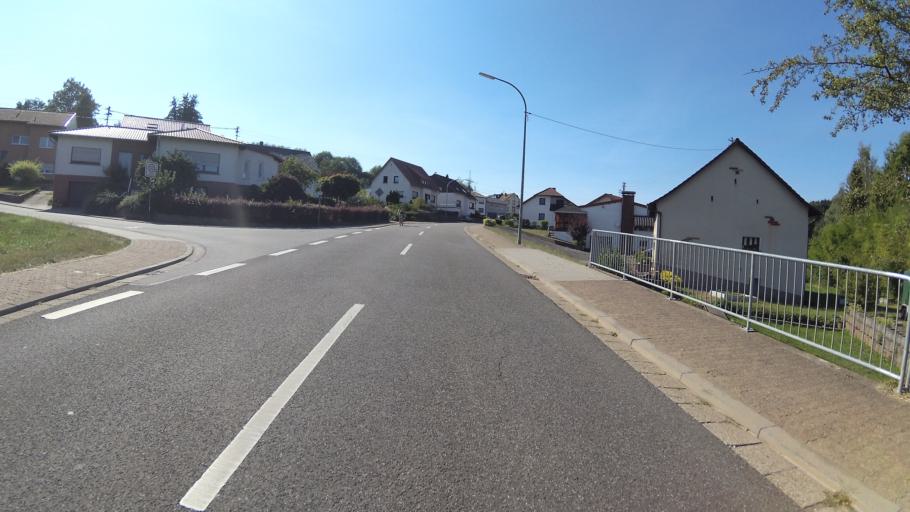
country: DE
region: Saarland
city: Eppelborn
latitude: 49.3766
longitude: 6.9697
